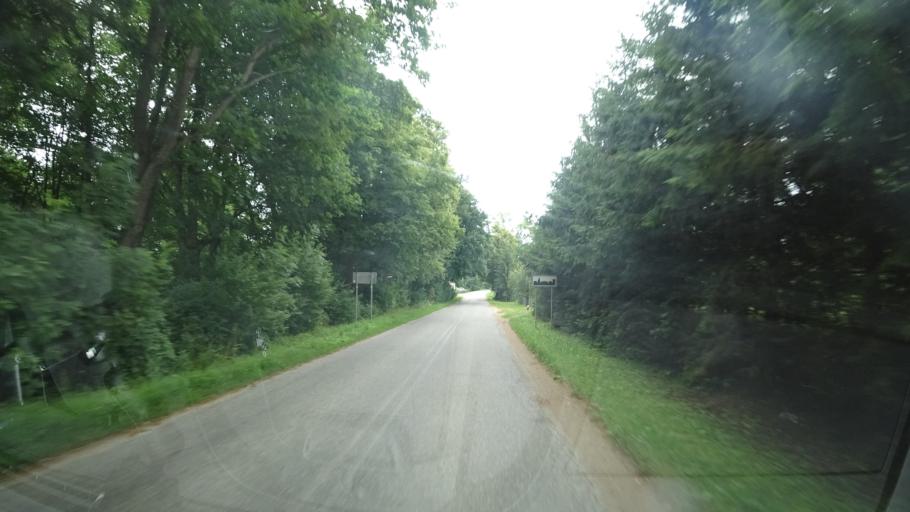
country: PL
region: Podlasie
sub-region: Powiat suwalski
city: Filipow
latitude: 54.2890
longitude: 22.5106
